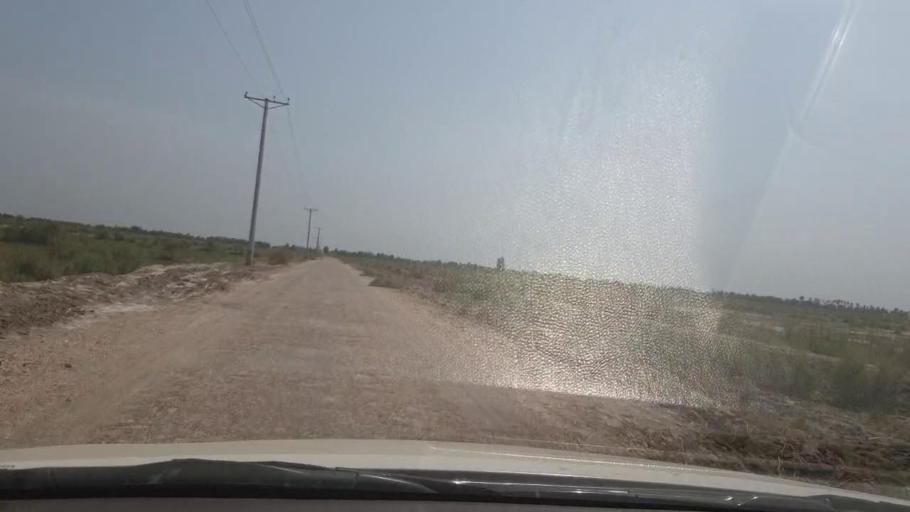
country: PK
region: Sindh
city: Garhi Yasin
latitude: 27.9846
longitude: 68.5022
